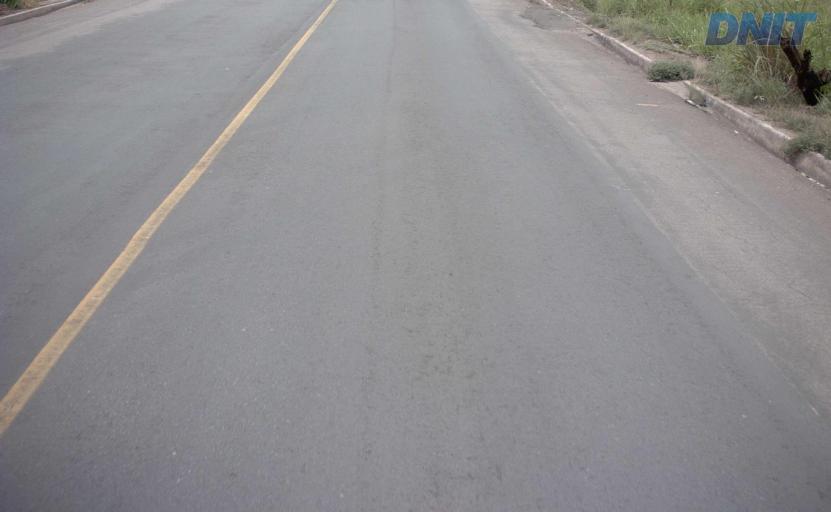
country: BR
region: Minas Gerais
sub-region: Coronel Fabriciano
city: Coronel Fabriciano
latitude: -19.5366
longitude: -42.6742
